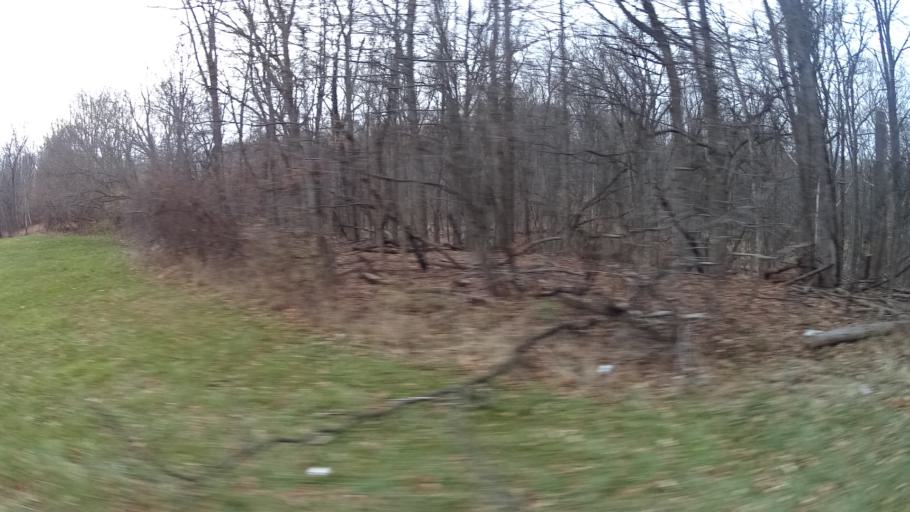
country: US
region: Ohio
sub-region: Lorain County
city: North Ridgeville
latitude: 41.3963
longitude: -82.0591
